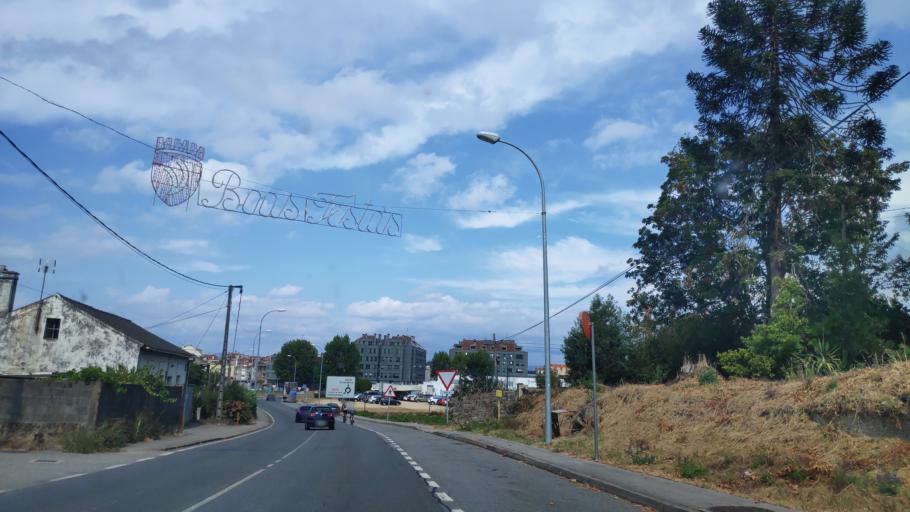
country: ES
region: Galicia
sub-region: Provincia de Pontevedra
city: Vilagarcia de Arousa
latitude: 42.5935
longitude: -8.7491
